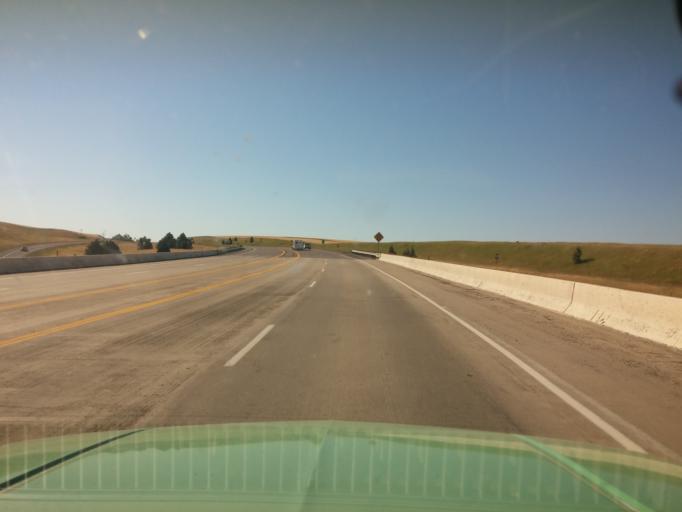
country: US
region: Washington
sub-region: Asotin County
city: Clarkston
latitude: 46.4744
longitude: -117.0374
